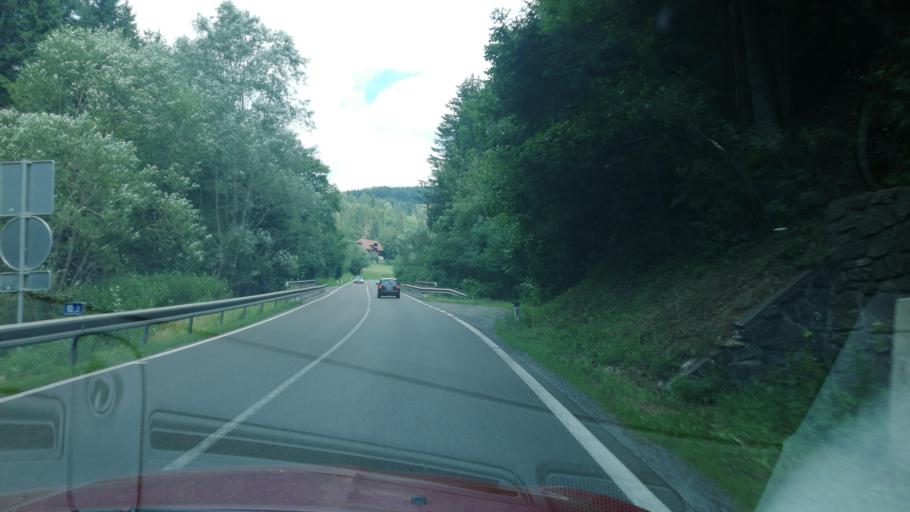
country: AT
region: Styria
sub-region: Politischer Bezirk Murau
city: Neumarkt in Steiermark
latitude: 47.0854
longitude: 14.4296
